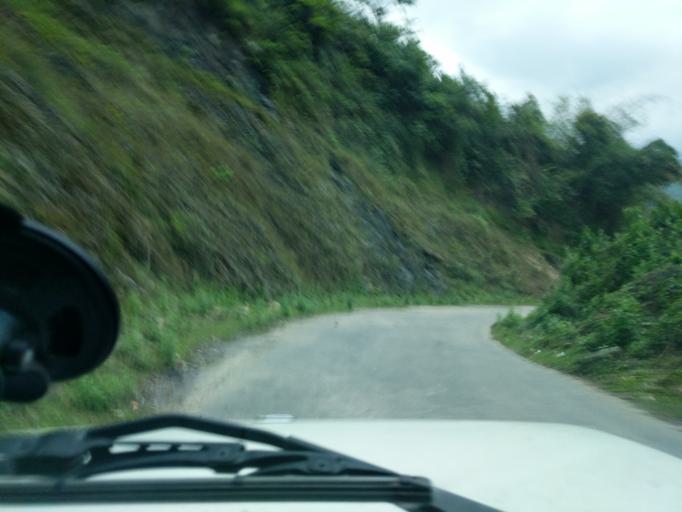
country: BT
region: Mongar
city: Mongar
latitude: 27.2948
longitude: 91.1534
